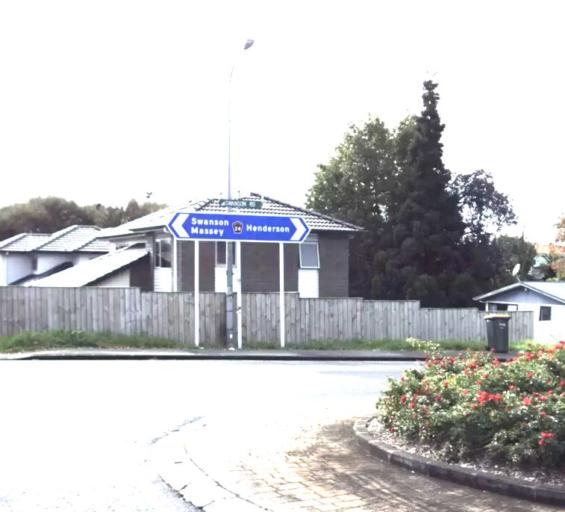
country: NZ
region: Auckland
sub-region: Auckland
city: Rosebank
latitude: -36.8619
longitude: 174.6130
